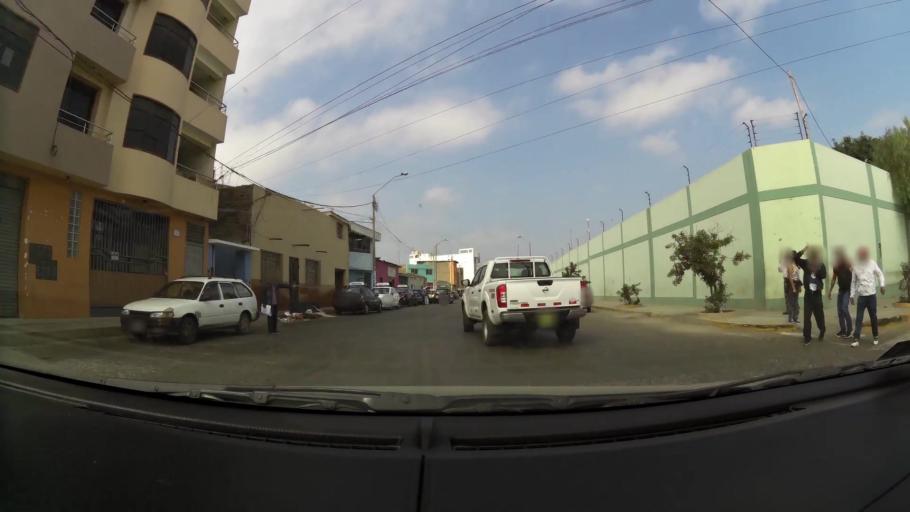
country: PE
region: La Libertad
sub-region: Provincia de Trujillo
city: Trujillo
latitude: -8.1167
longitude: -79.0202
